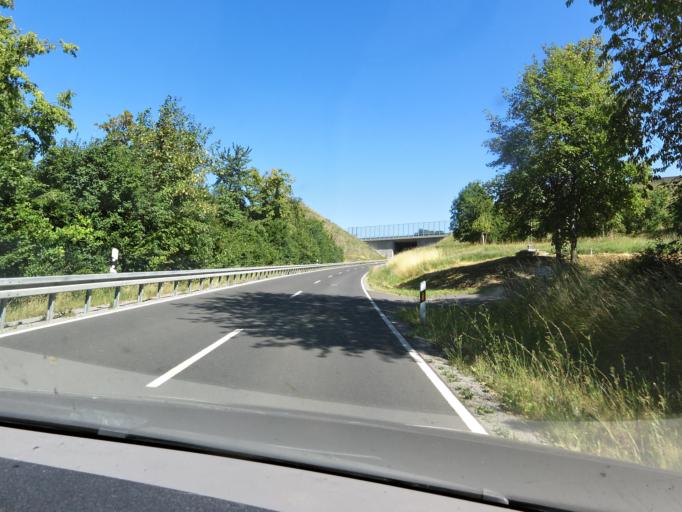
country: DE
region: Bavaria
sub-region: Regierungsbezirk Unterfranken
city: Theilheim
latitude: 49.7530
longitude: 10.0411
